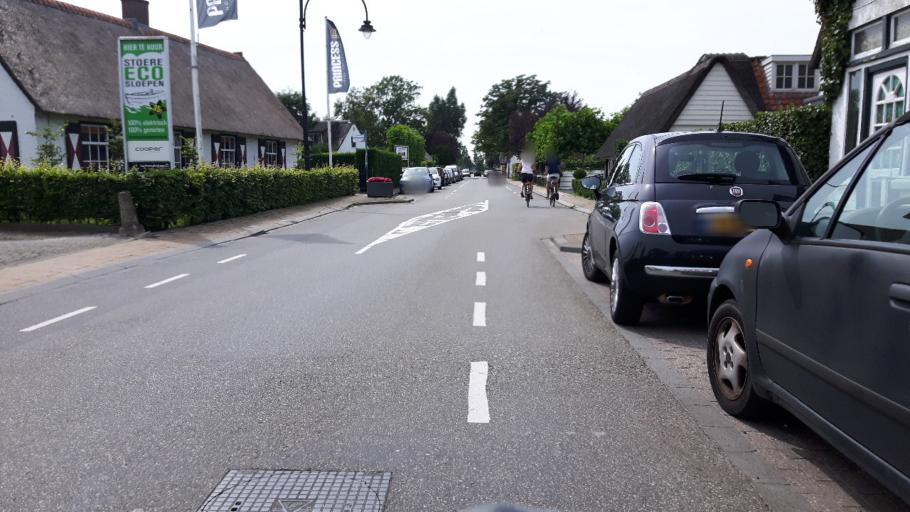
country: NL
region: North Holland
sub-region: Gemeente Wijdemeren
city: Oud-Loosdrecht
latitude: 52.2071
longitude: 5.0737
